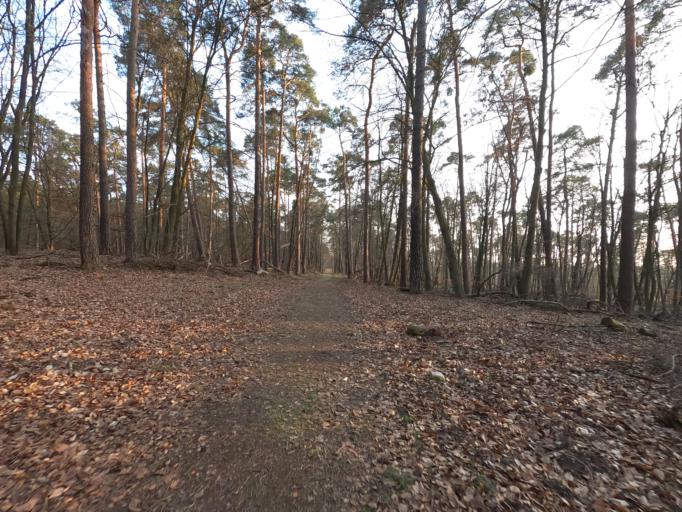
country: DE
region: Hesse
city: Kelsterbach
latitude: 50.0251
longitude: 8.5106
